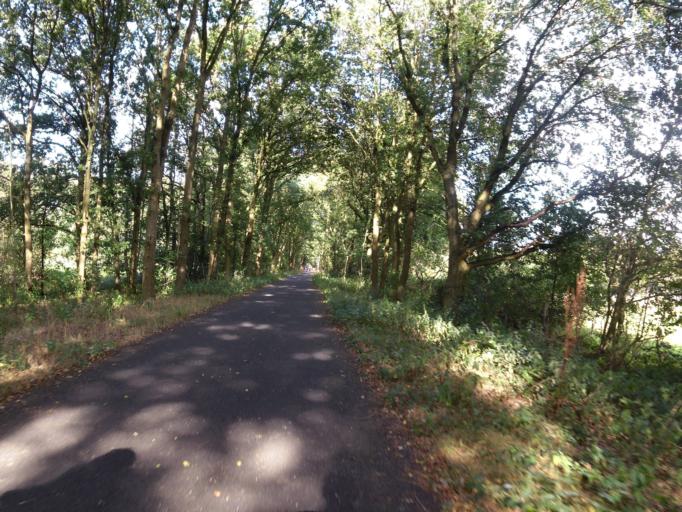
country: NL
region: North Brabant
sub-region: Gemeente Heeze-Leende
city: Heeze
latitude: 51.3772
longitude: 5.5449
